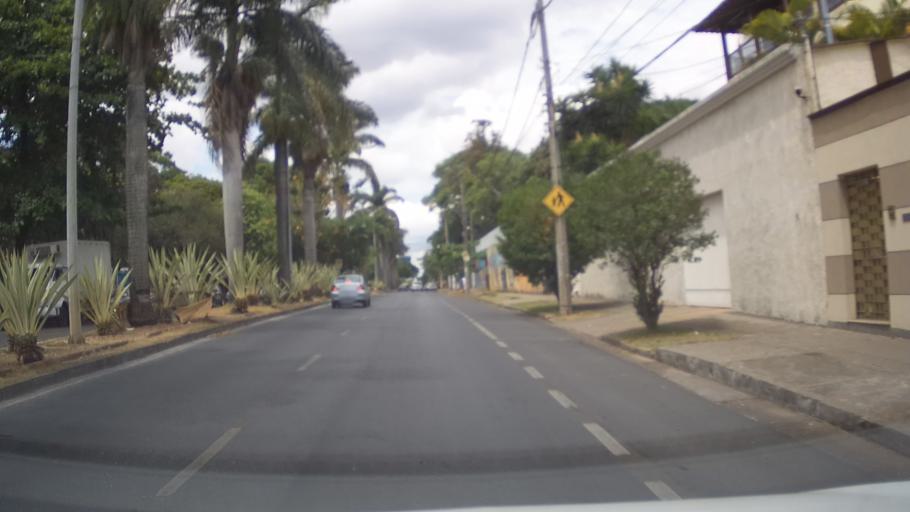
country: BR
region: Minas Gerais
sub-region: Belo Horizonte
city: Belo Horizonte
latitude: -19.8536
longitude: -43.9656
